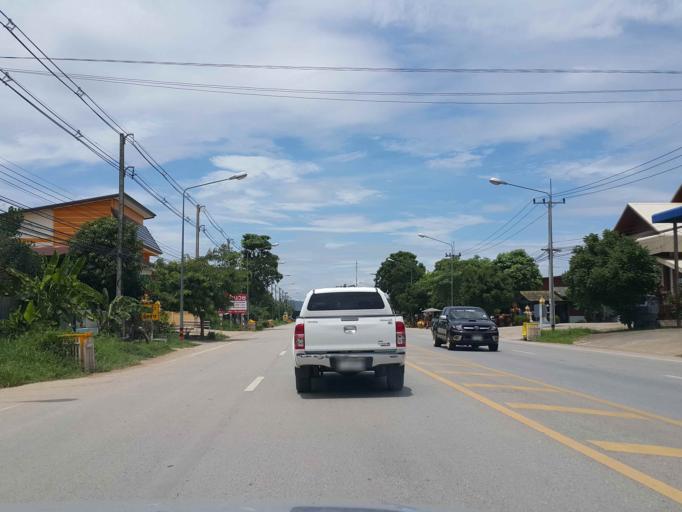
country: TH
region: Sukhothai
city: Ban Na
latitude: 17.0141
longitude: 99.7547
